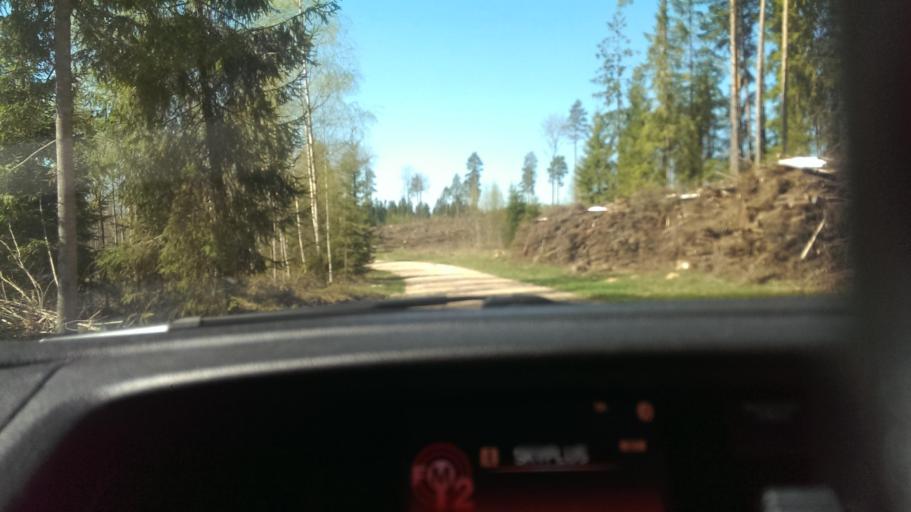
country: EE
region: Vorumaa
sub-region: Antsla vald
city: Vana-Antsla
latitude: 58.0173
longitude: 26.7468
